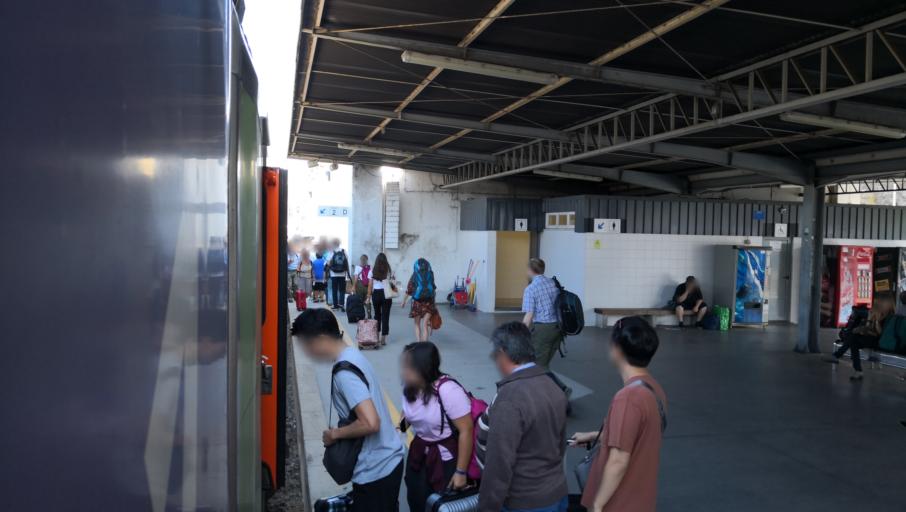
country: PT
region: Coimbra
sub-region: Coimbra
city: Coimbra
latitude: 40.2249
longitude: -8.4405
